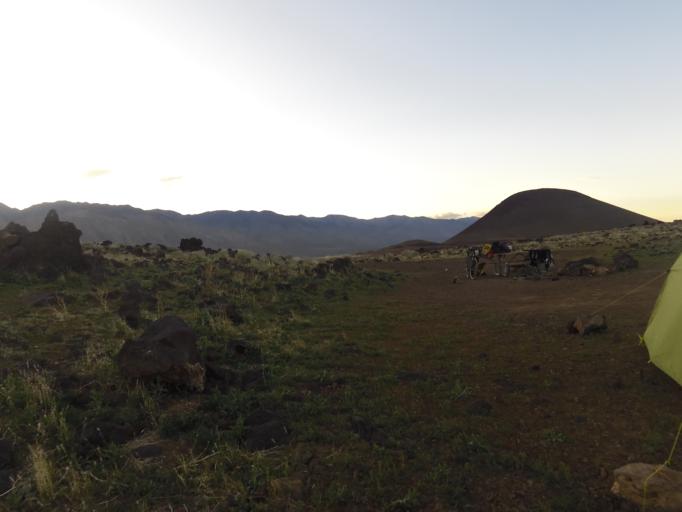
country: US
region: California
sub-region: Kern County
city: Inyokern
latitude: 35.9730
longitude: -117.9104
